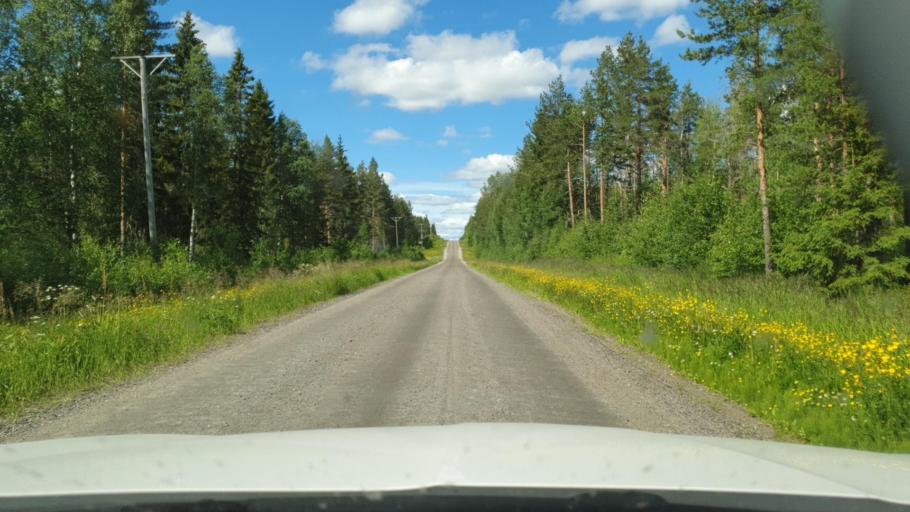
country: SE
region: Vaesterbotten
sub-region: Skelleftea Kommun
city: Backa
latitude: 65.1722
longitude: 21.1046
